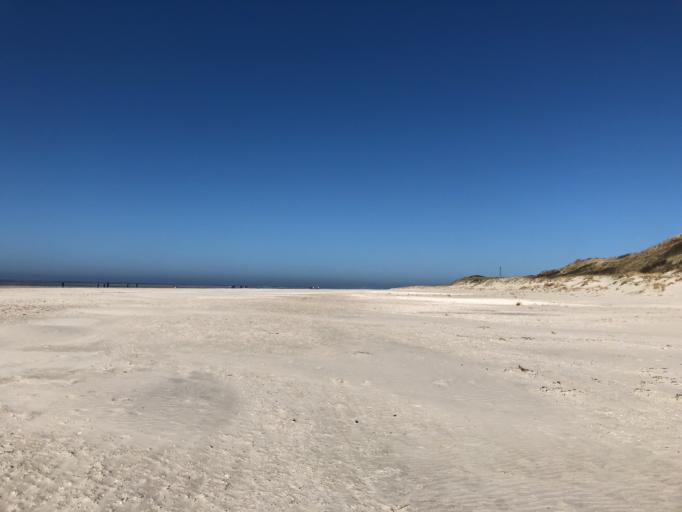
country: DK
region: South Denmark
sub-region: Varde Kommune
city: Oksbol
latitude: 55.5553
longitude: 8.0841
